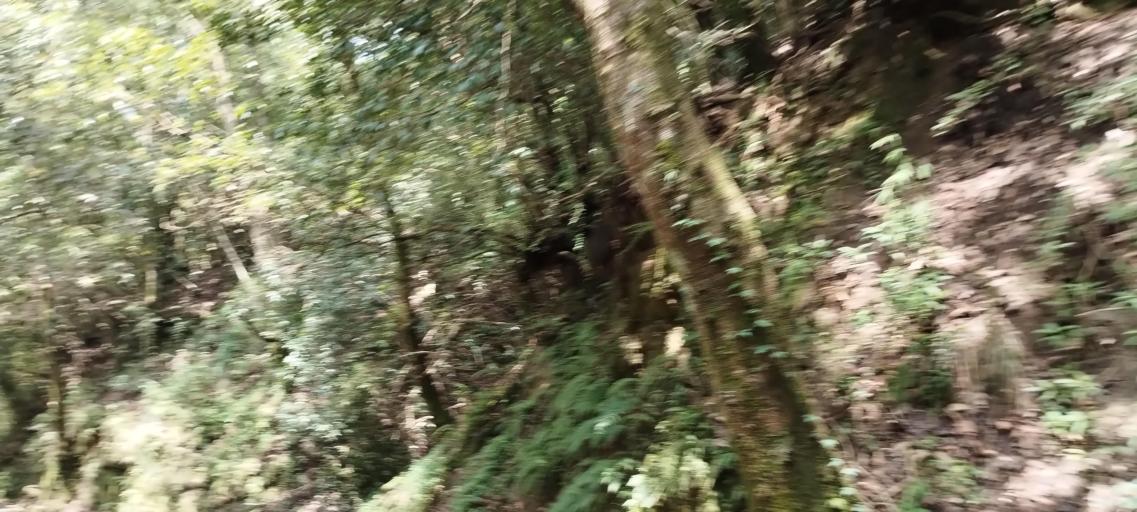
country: NP
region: Central Region
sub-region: Bagmati Zone
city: Kathmandu
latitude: 27.7900
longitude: 85.3747
